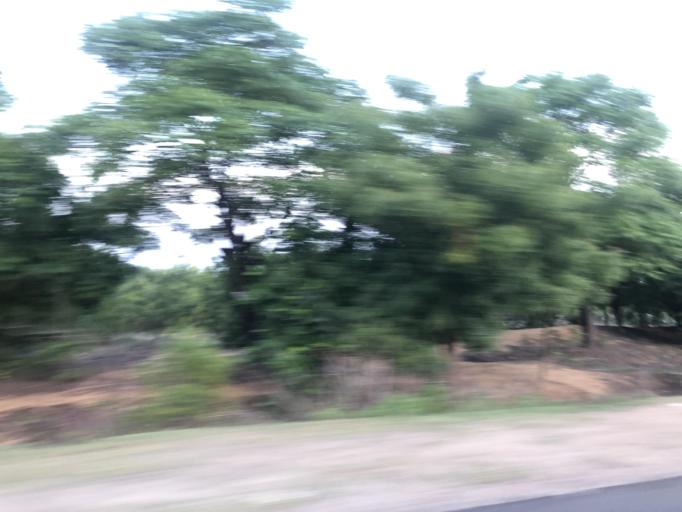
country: IN
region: Tamil Nadu
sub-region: Kancheepuram
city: Mamallapuram
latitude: 12.7610
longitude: 80.2447
